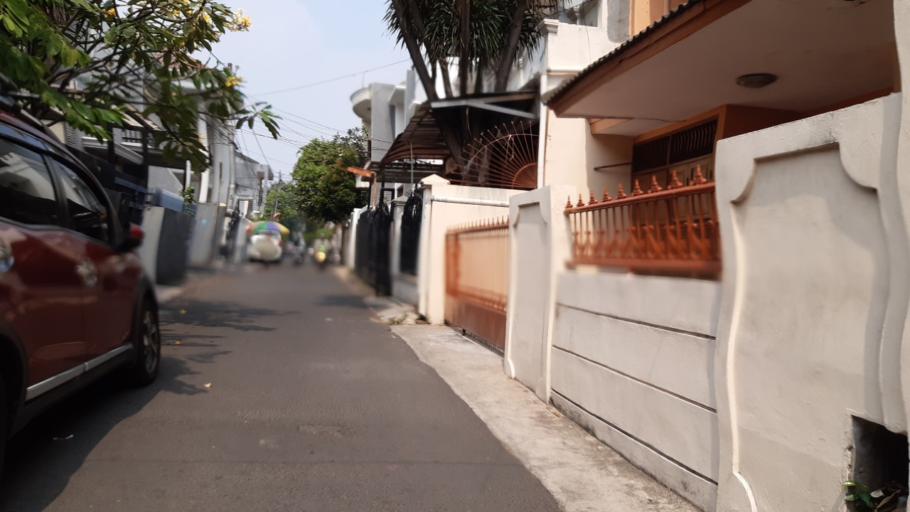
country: ID
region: Jakarta Raya
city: Jakarta
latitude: -6.2346
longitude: 106.8574
